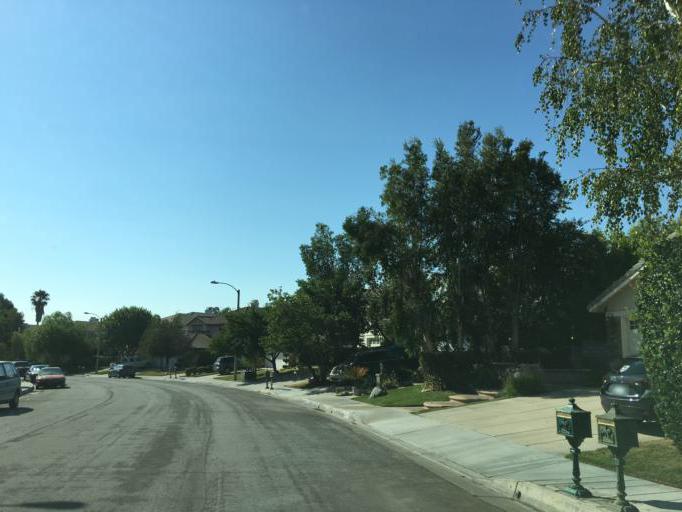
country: US
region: California
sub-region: Los Angeles County
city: Santa Clarita
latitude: 34.3854
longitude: -118.5911
